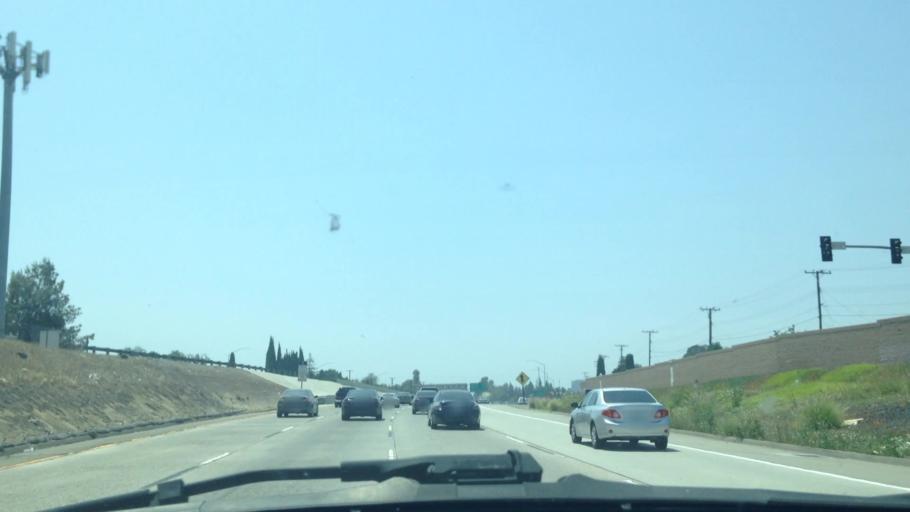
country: US
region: California
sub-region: Orange County
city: Orange
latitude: 33.7771
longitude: -117.8368
